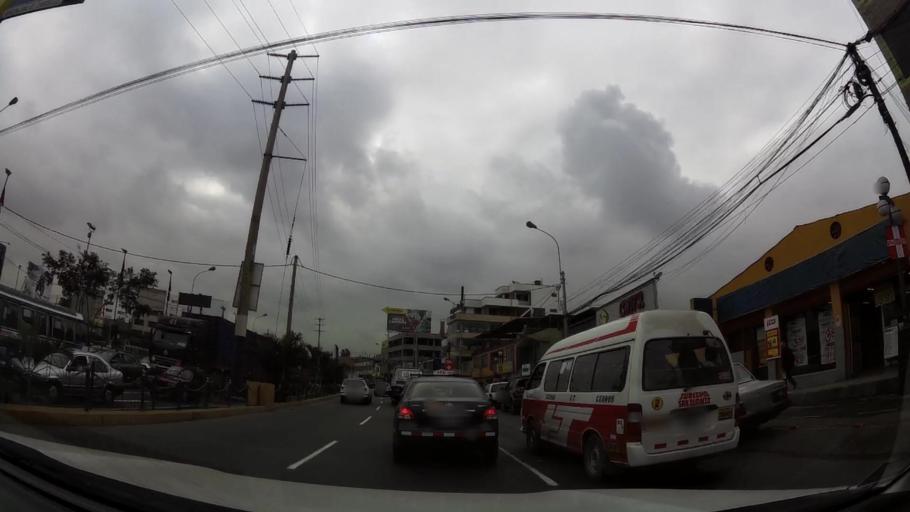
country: PE
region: Lima
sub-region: Lima
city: Surco
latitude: -12.1833
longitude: -77.0001
